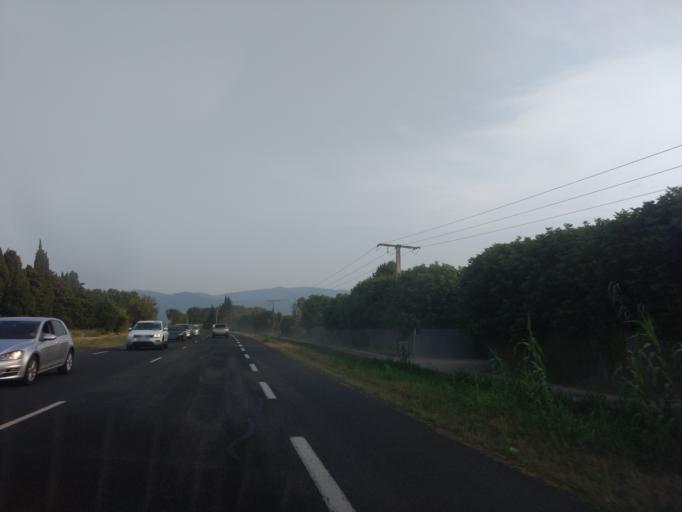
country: FR
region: Languedoc-Roussillon
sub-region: Departement des Pyrenees-Orientales
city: Latour-Bas-Elne
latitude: 42.6033
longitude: 3.0242
